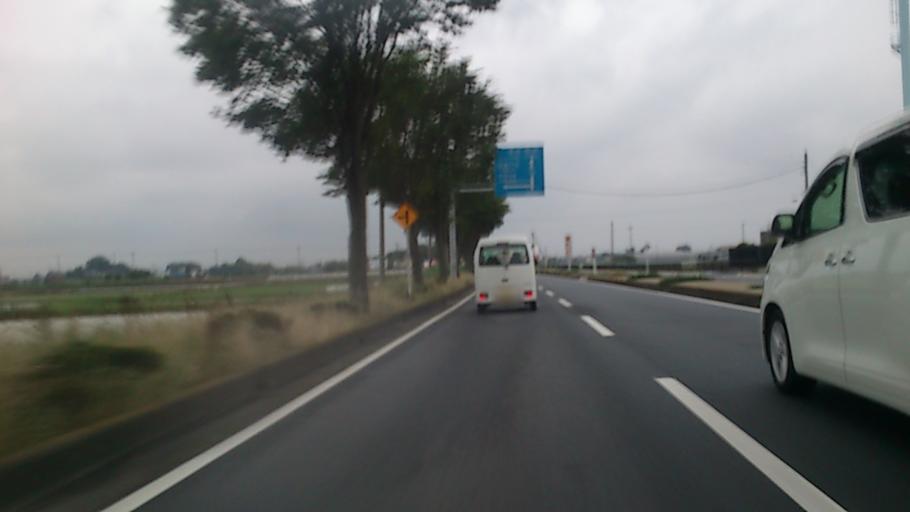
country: JP
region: Saitama
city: Hanyu
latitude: 36.1562
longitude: 139.4966
